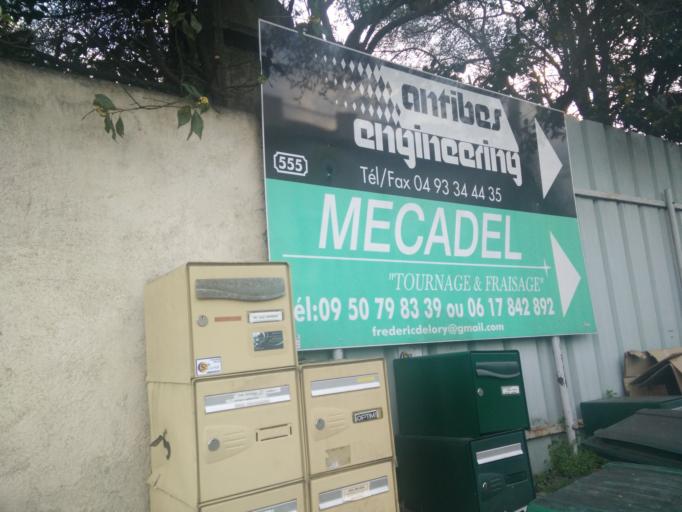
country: FR
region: Provence-Alpes-Cote d'Azur
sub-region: Departement des Alpes-Maritimes
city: Antibes
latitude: 43.5920
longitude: 7.1159
